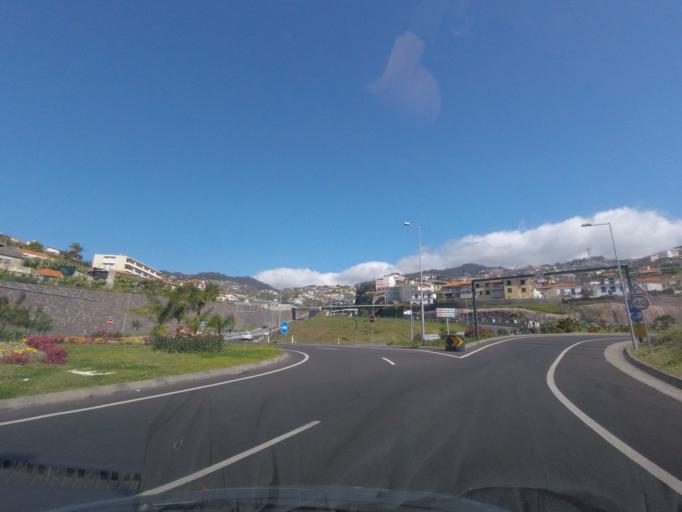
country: PT
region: Madeira
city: Camara de Lobos
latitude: 32.6547
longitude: -16.9673
